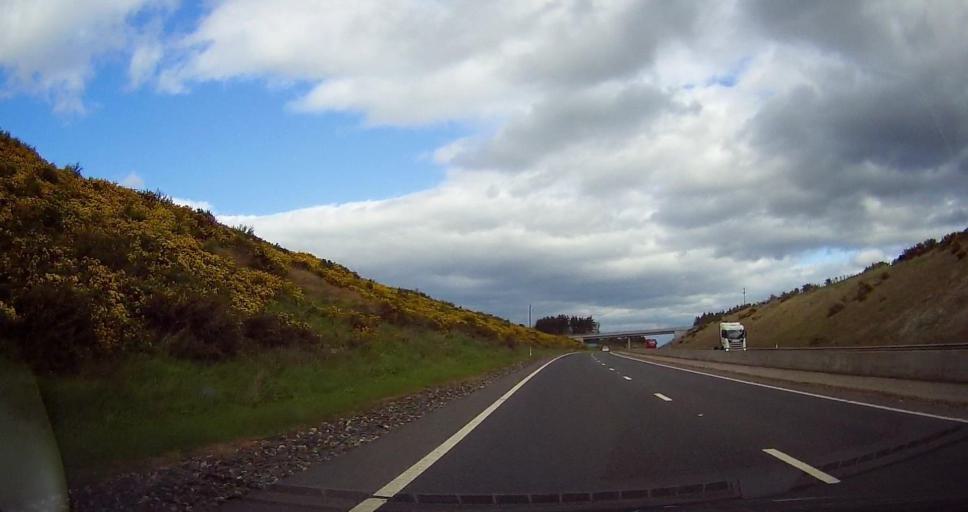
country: GB
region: Scotland
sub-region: Aberdeen City
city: Cults
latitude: 57.0791
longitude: -2.1897
